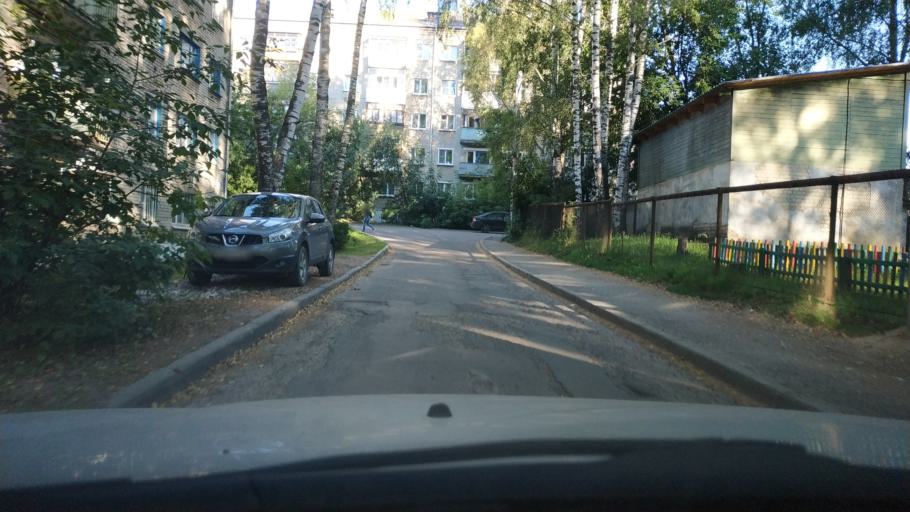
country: RU
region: Kostroma
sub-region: Kostromskoy Rayon
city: Kostroma
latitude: 57.7513
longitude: 40.9133
